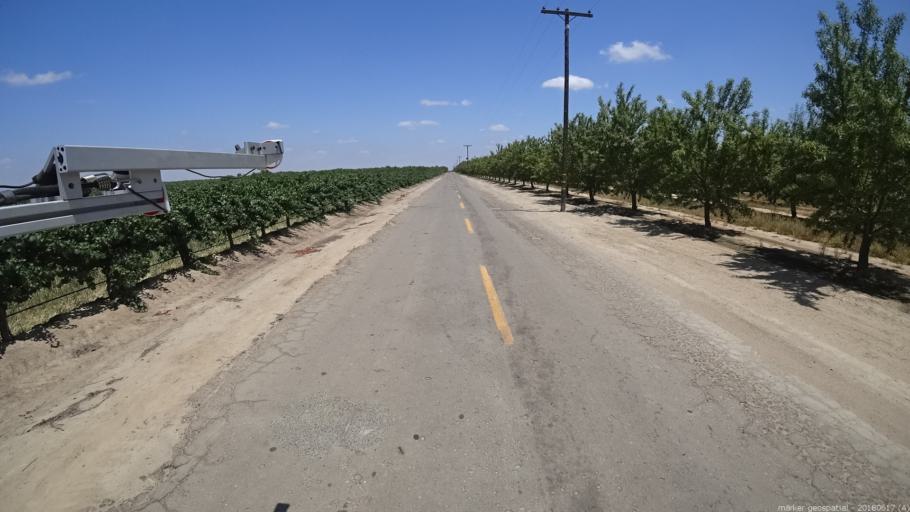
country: US
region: California
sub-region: Fresno County
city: Kerman
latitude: 36.8294
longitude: -120.1587
